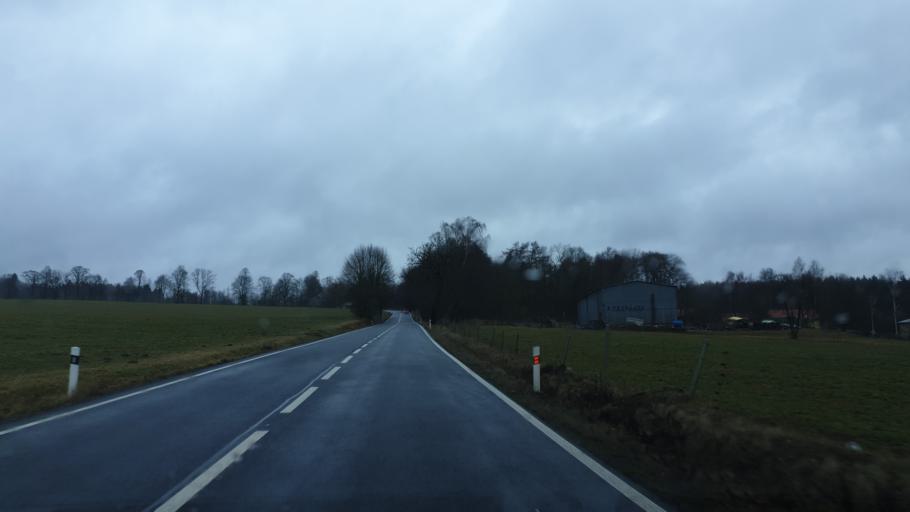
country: CZ
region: Karlovarsky
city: As
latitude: 50.2466
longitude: 12.1823
